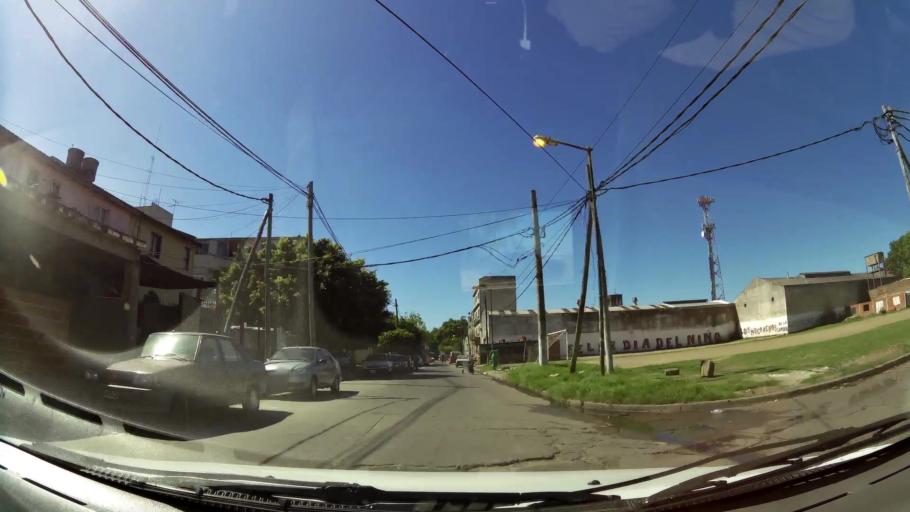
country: AR
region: Buenos Aires
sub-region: Partido de General San Martin
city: General San Martin
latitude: -34.5545
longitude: -58.5246
